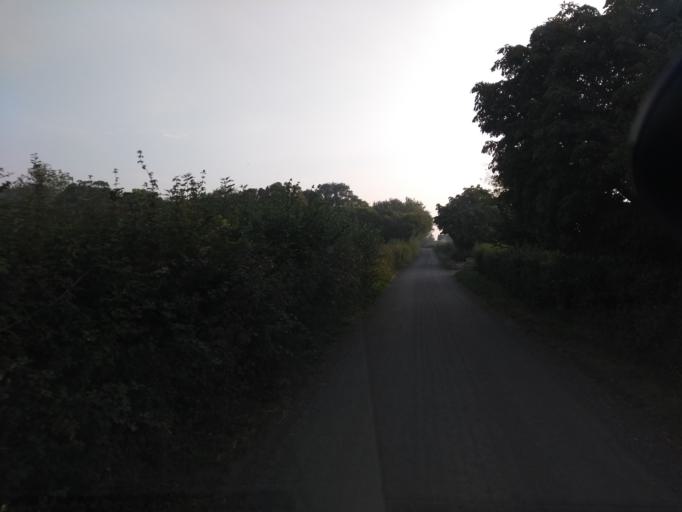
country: GB
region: England
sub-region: Somerset
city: Ilminster
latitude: 50.9922
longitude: -2.9284
